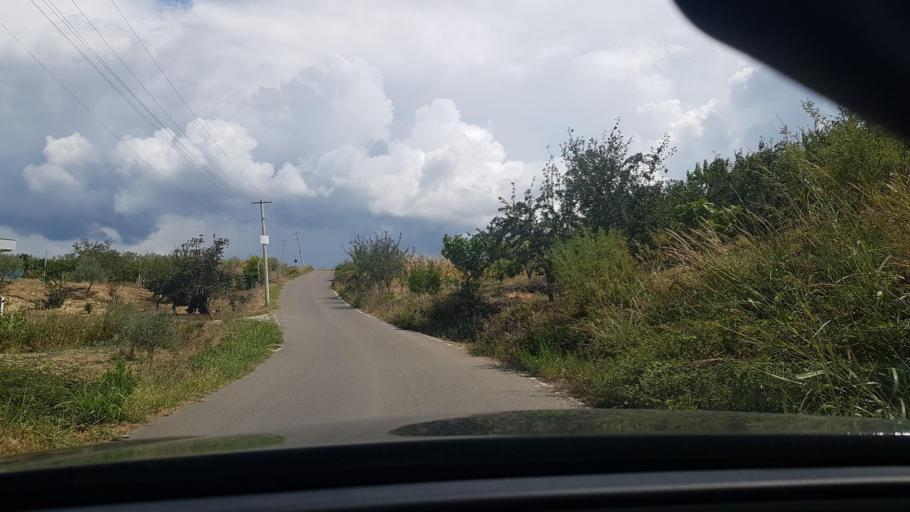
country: AL
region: Durres
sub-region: Rrethi i Durresit
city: Rrashbull
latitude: 41.2958
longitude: 19.5285
